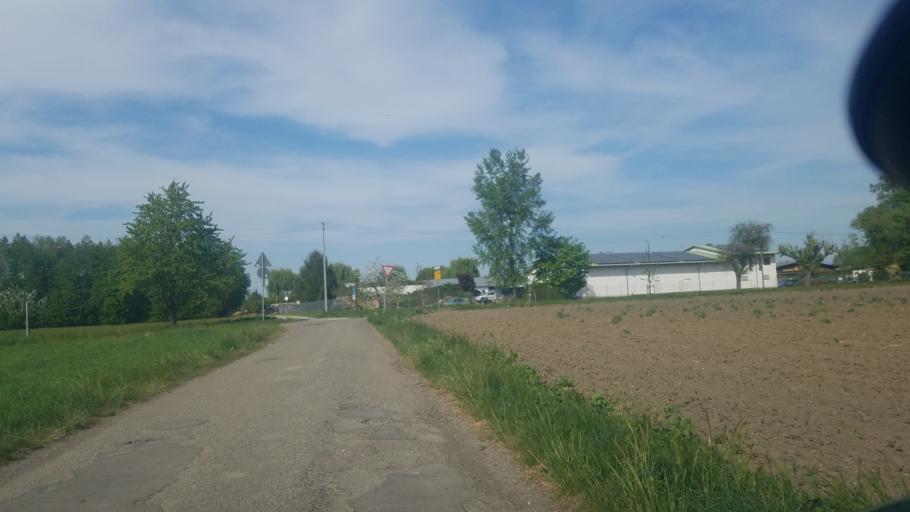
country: DE
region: Baden-Wuerttemberg
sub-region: Freiburg Region
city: Meissenheim
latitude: 48.4387
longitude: 7.7927
